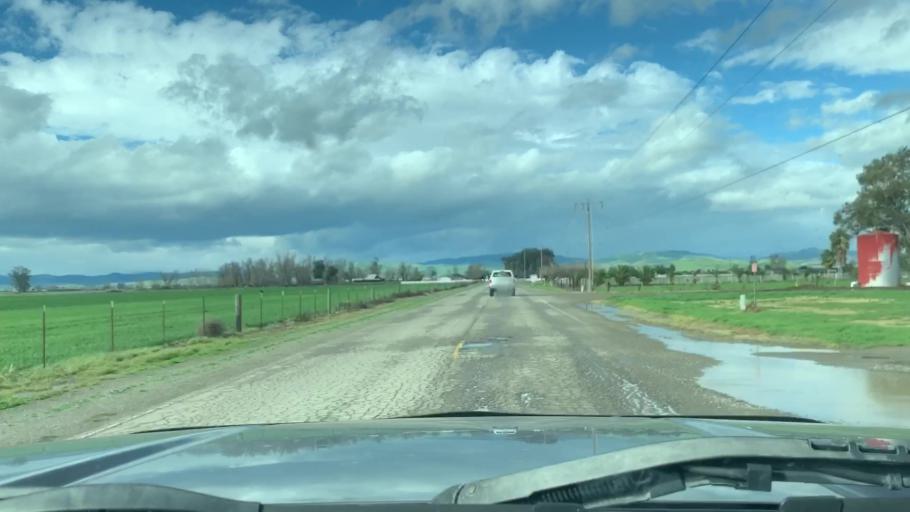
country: US
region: California
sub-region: Merced County
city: Los Banos
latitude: 37.1221
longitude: -120.9684
